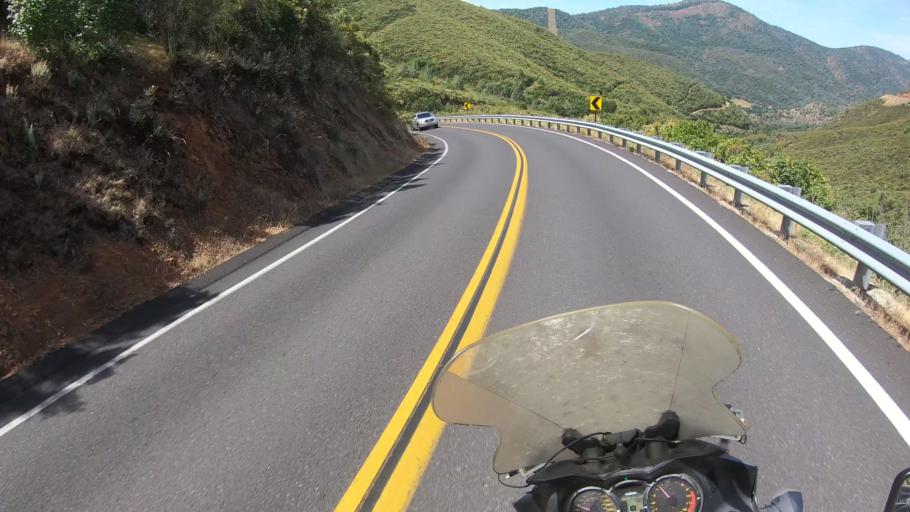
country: US
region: California
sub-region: Tuolumne County
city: Tuolumne City
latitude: 37.8186
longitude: -120.2849
